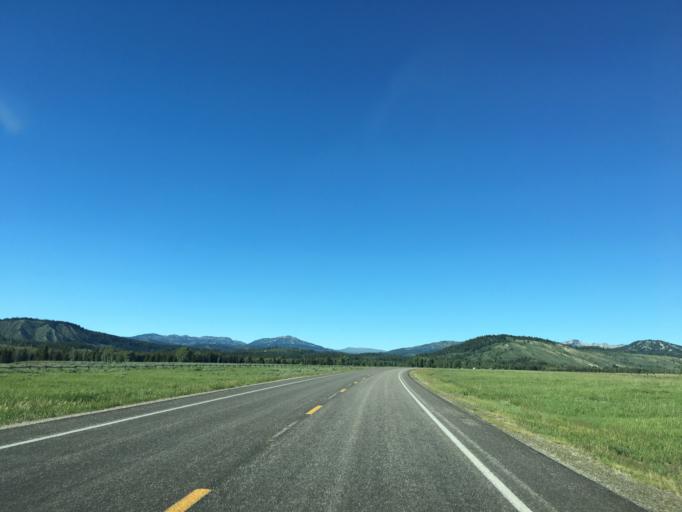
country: US
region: Wyoming
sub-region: Teton County
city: Jackson
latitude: 43.8195
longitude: -110.5236
